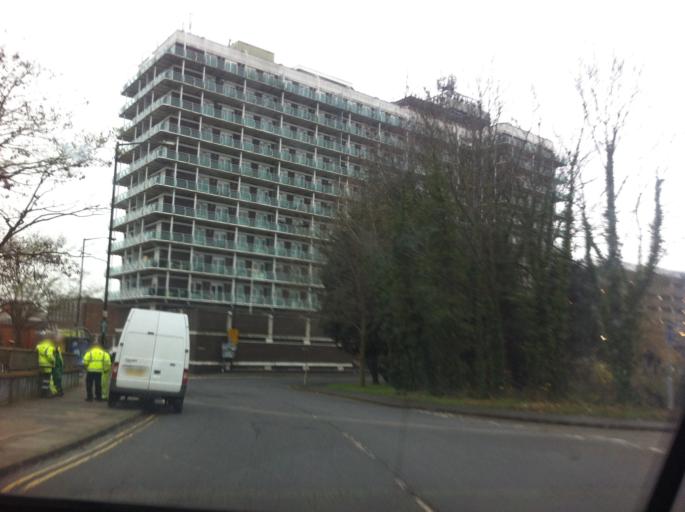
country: GB
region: England
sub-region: Northamptonshire
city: Earls Barton
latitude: 52.2722
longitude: -0.7610
